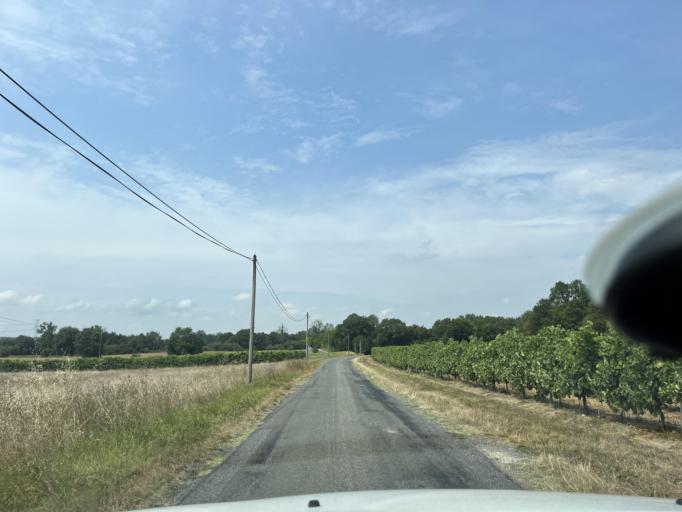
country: FR
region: Poitou-Charentes
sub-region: Departement de la Charente-Maritime
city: Pons
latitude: 45.6047
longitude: -0.5956
